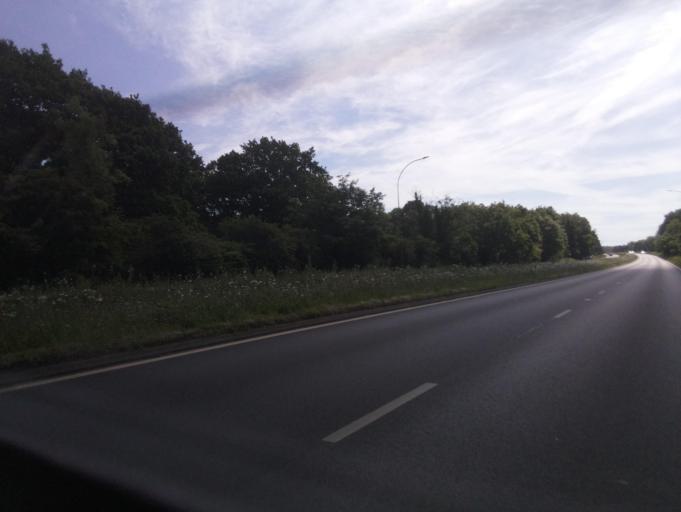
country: GB
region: England
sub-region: North Lincolnshire
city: Manton
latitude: 53.5599
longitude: -0.5958
